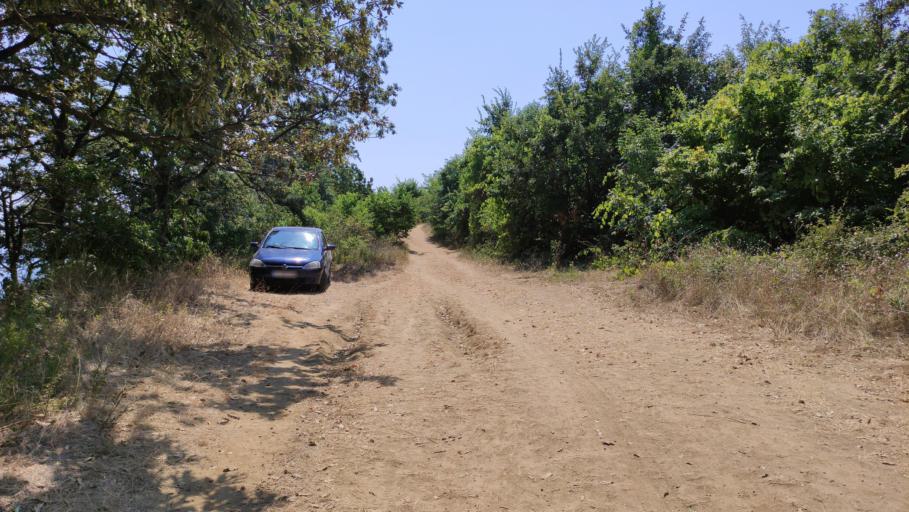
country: BG
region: Varna
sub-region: Obshtina Byala
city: Byala
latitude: 42.8606
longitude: 27.8993
